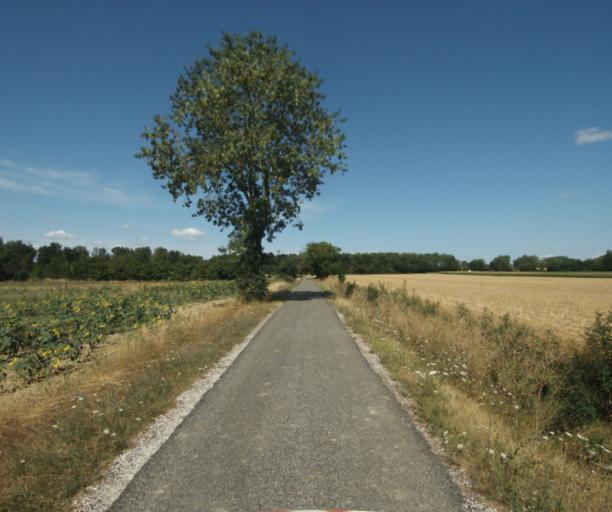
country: FR
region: Midi-Pyrenees
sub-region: Departement de la Haute-Garonne
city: Revel
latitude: 43.4930
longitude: 1.9630
